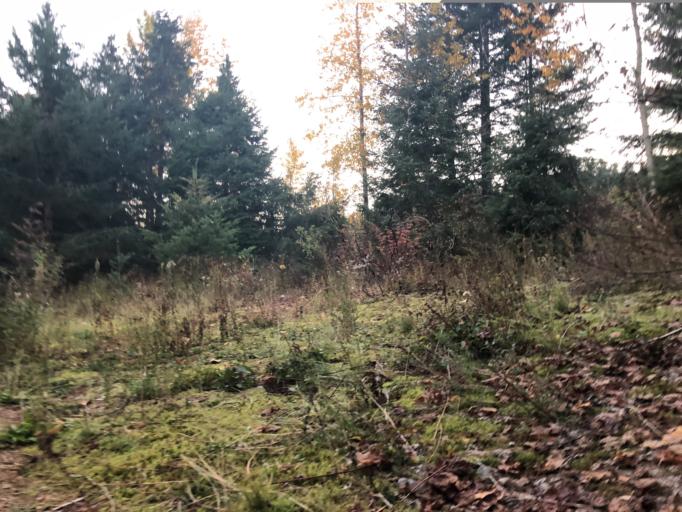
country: US
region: Washington
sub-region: King County
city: Tanner
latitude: 47.3994
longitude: -121.3810
